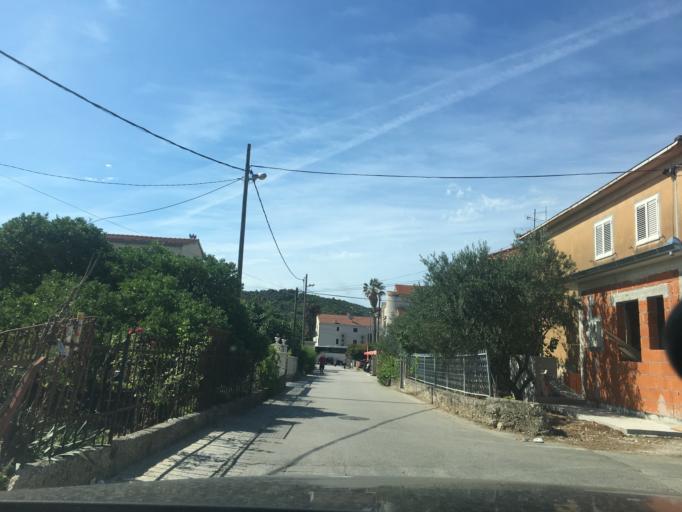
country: HR
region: Splitsko-Dalmatinska
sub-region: Grad Trogir
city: Trogir
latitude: 43.5198
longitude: 16.2538
